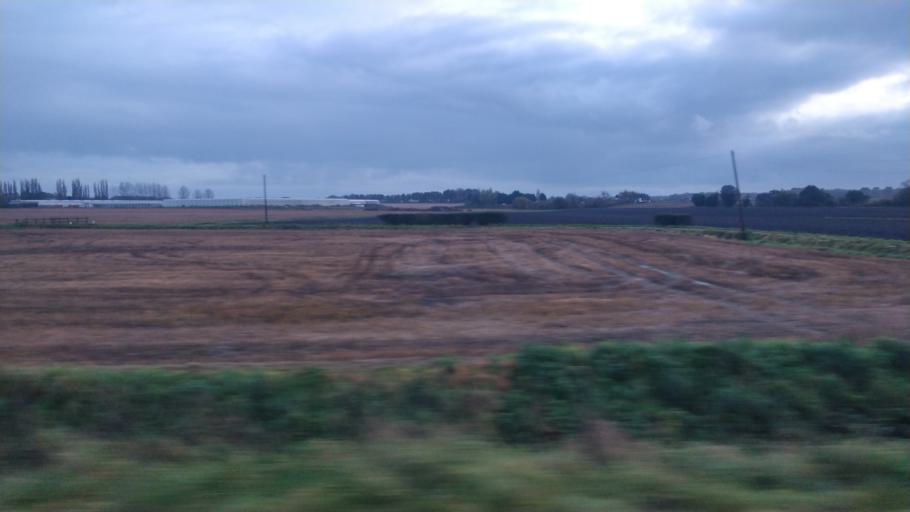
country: GB
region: England
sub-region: Lancashire
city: Ormskirk
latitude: 53.6174
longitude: -2.8895
